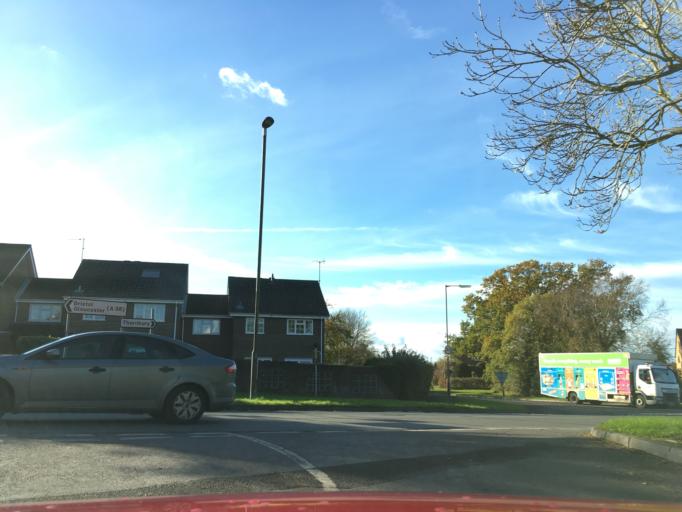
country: GB
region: England
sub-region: South Gloucestershire
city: Thornbury
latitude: 51.6102
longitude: -2.5052
